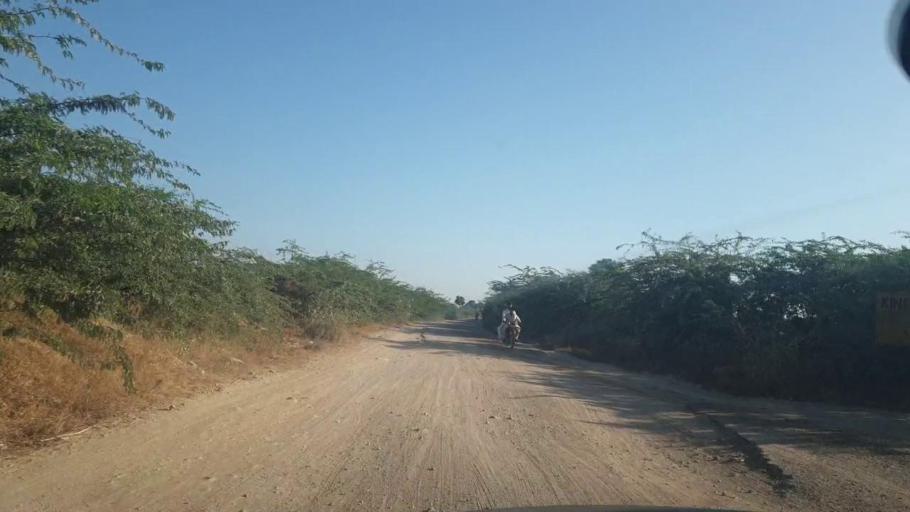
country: PK
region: Sindh
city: Malir Cantonment
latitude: 25.1077
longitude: 67.2625
